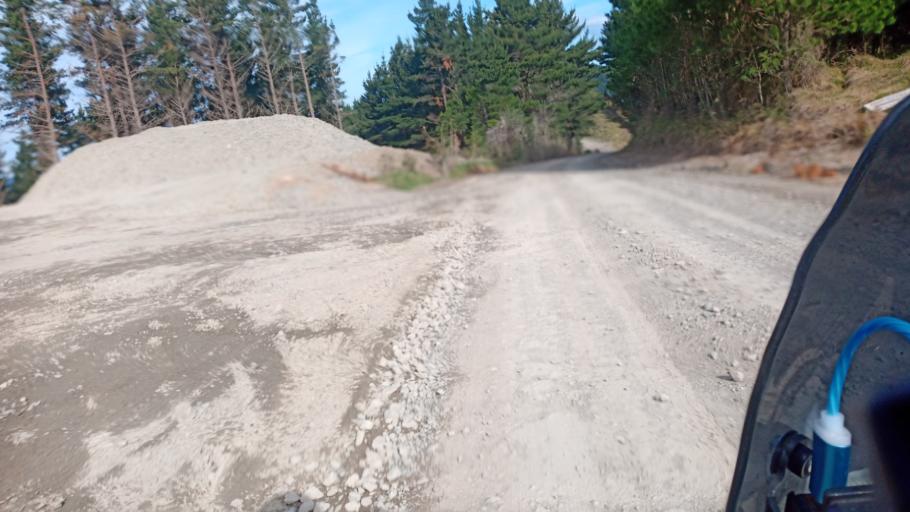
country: NZ
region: Gisborne
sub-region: Gisborne District
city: Gisborne
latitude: -38.1217
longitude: 178.1575
